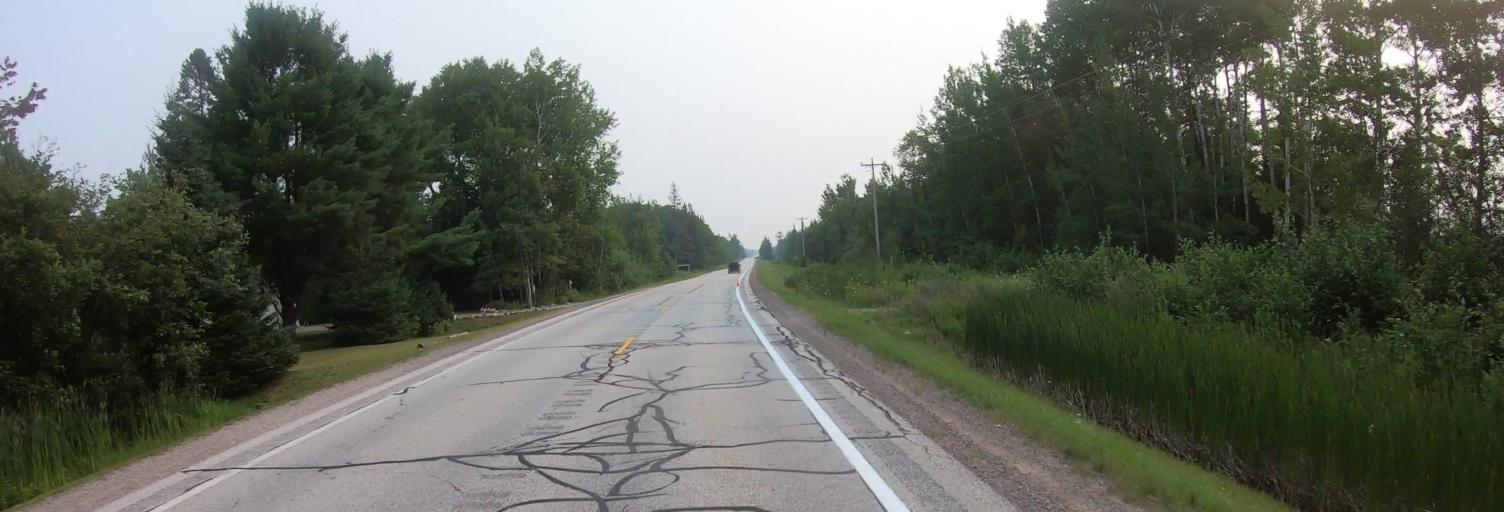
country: US
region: Michigan
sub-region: Luce County
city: Newberry
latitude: 46.5112
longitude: -85.0898
